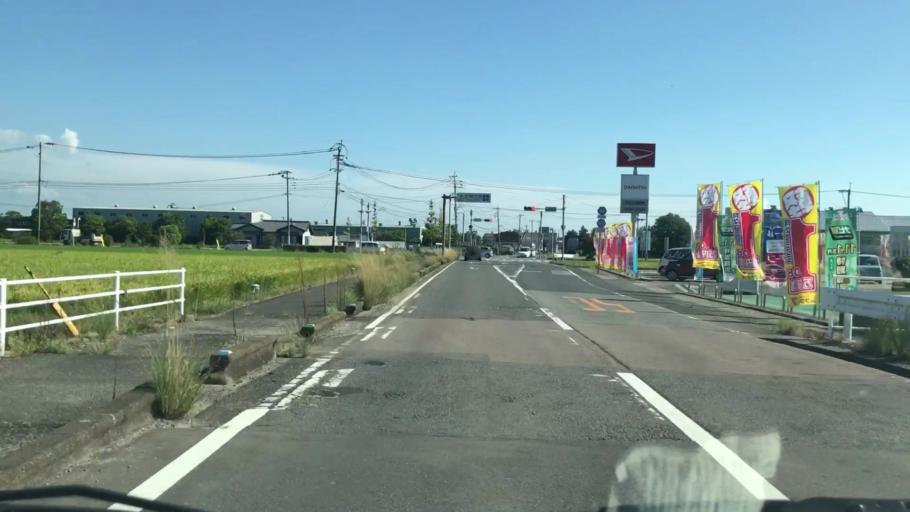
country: JP
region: Saga Prefecture
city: Okawa
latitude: 33.2137
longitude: 130.3353
